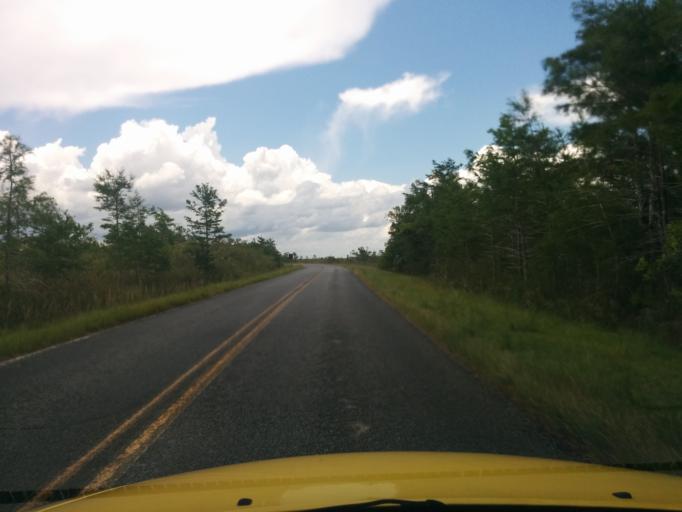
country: US
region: Florida
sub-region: Miami-Dade County
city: Florida City
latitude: 25.4373
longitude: -80.7817
